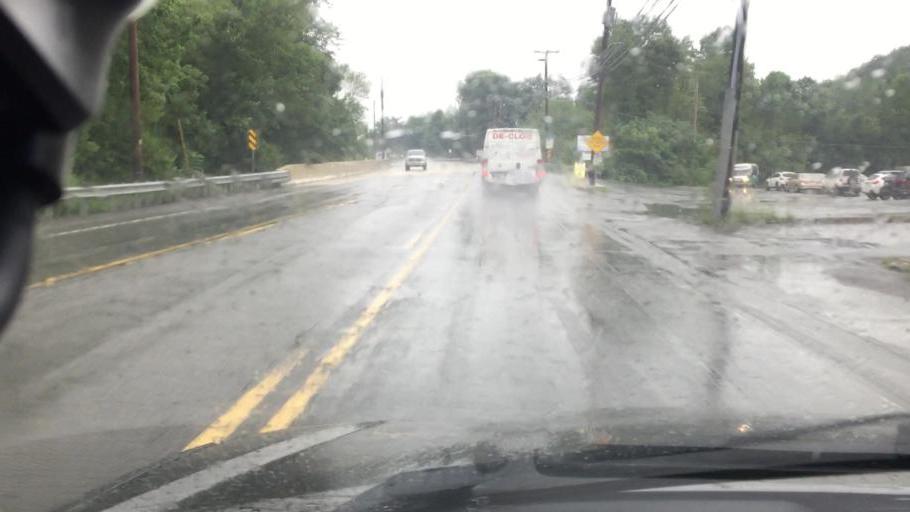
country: US
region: Pennsylvania
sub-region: Monroe County
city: Tannersville
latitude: 41.0069
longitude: -75.2839
